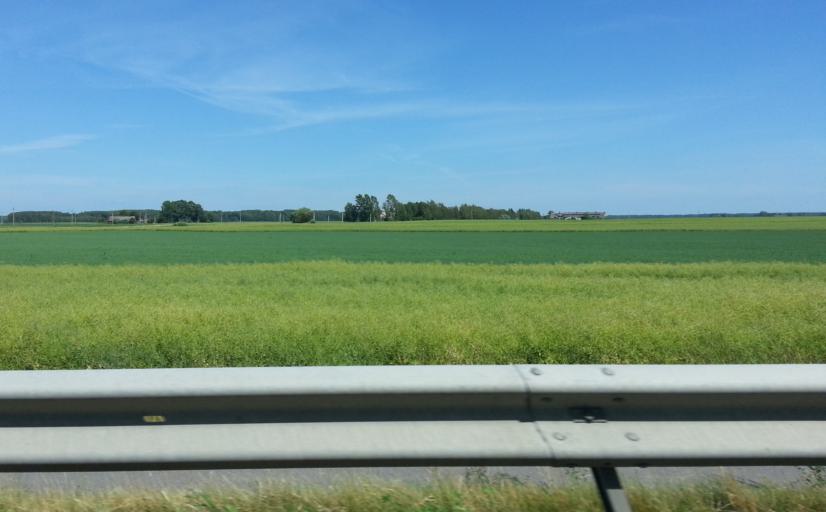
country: LT
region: Panevezys
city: Pasvalys
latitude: 56.1937
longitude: 24.4322
